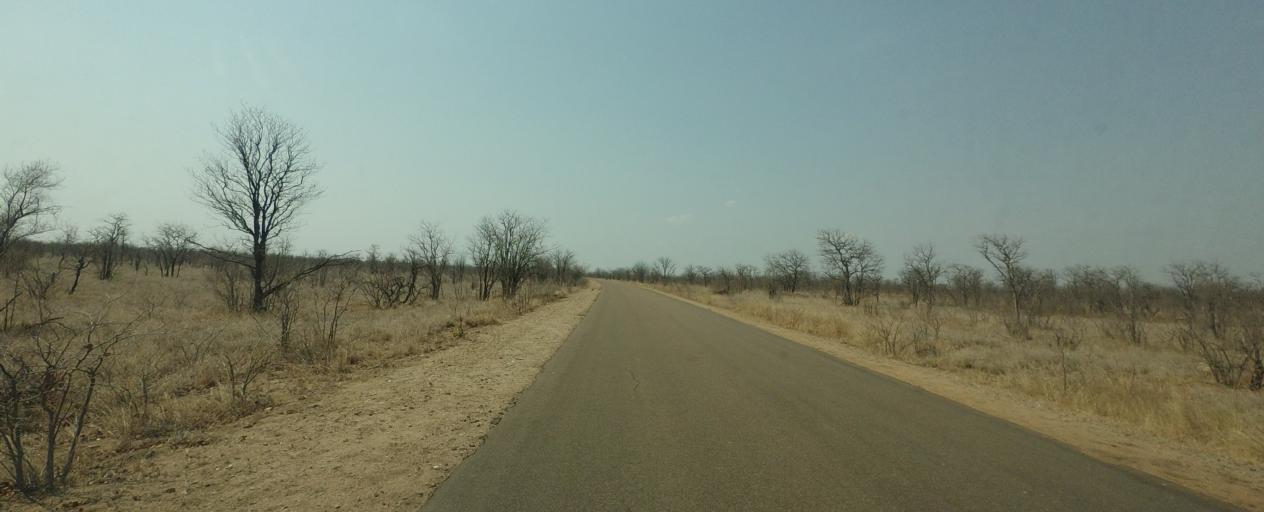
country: ZA
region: Limpopo
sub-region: Mopani District Municipality
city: Giyani
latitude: -23.3413
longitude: 31.3218
